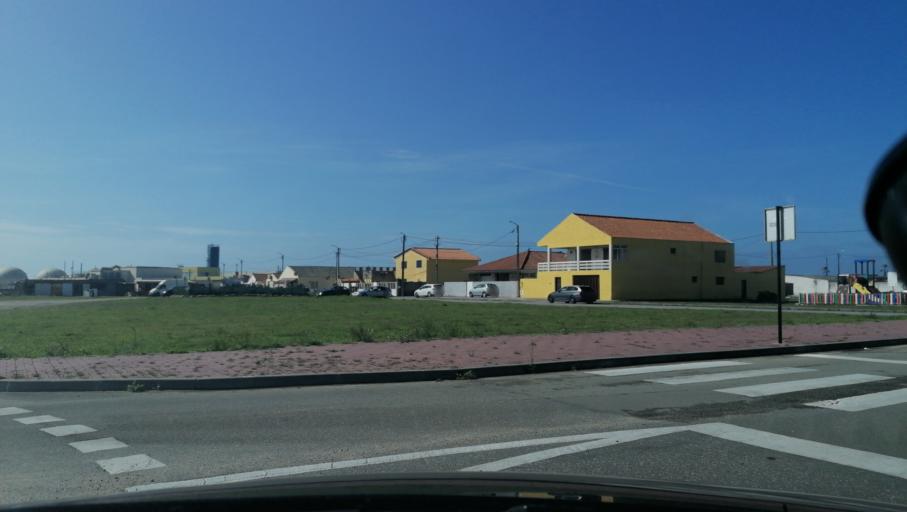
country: PT
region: Aveiro
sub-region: Espinho
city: Souto
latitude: 40.9776
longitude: -8.6466
